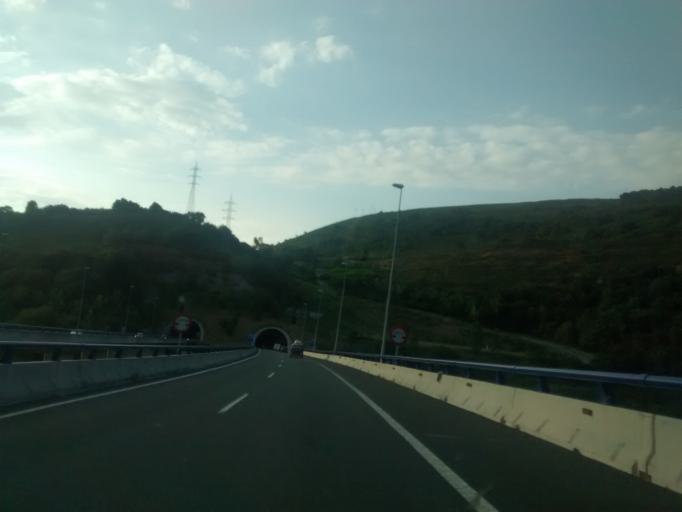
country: ES
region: Cantabria
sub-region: Provincia de Cantabria
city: Los Corrales de Buelna
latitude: 43.2244
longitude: -4.0788
